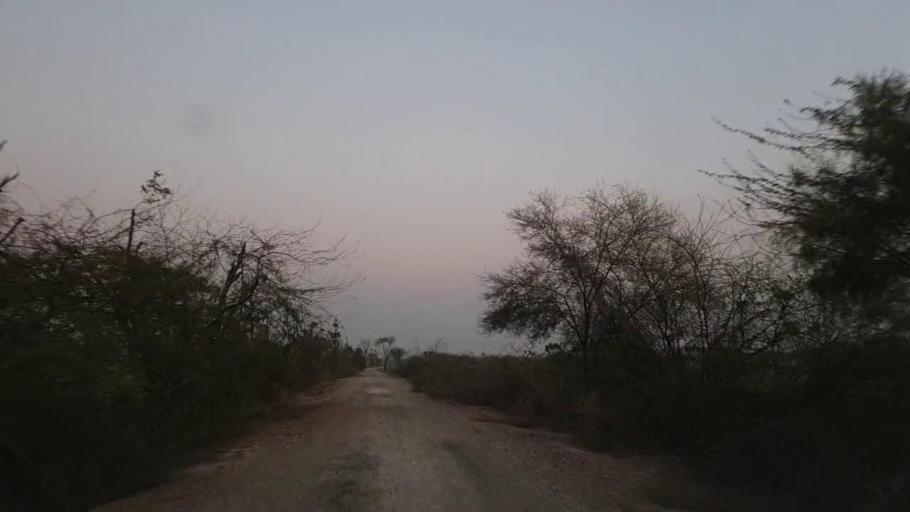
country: PK
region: Sindh
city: Bandhi
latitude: 26.6084
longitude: 68.3844
